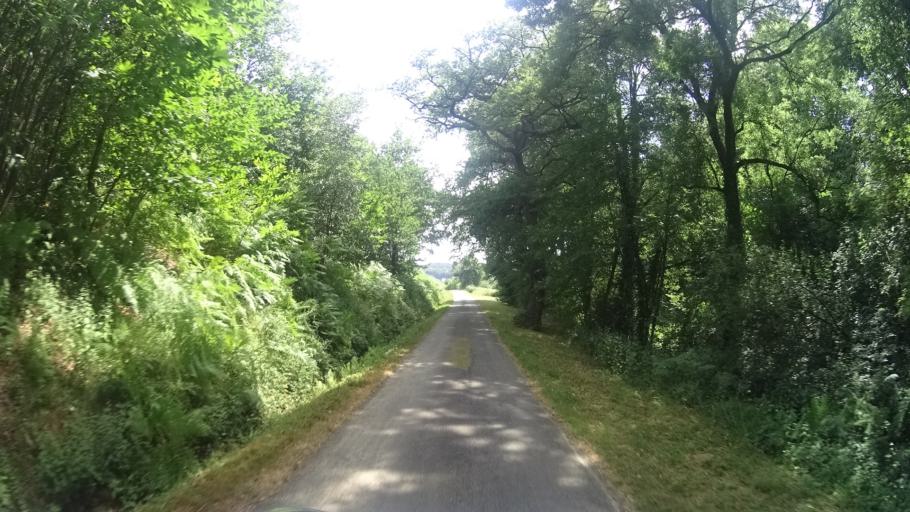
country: FR
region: Brittany
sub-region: Departement du Morbihan
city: Peillac
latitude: 47.7076
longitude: -2.2171
